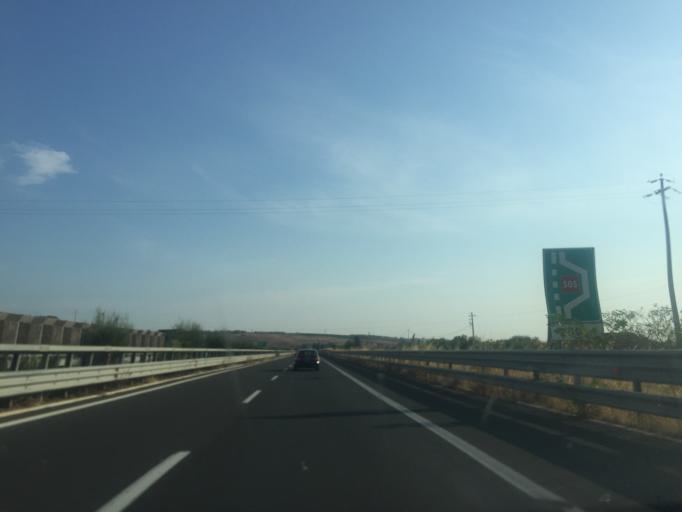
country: IT
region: Sicily
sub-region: Provincia di Siracusa
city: Carlentini
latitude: 37.3485
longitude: 15.0447
